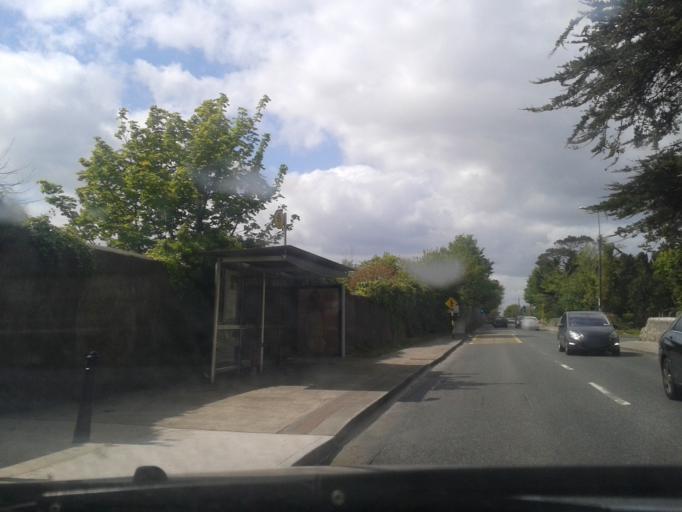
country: IE
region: Leinster
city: Sallynoggin
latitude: 53.2735
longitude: -6.1475
